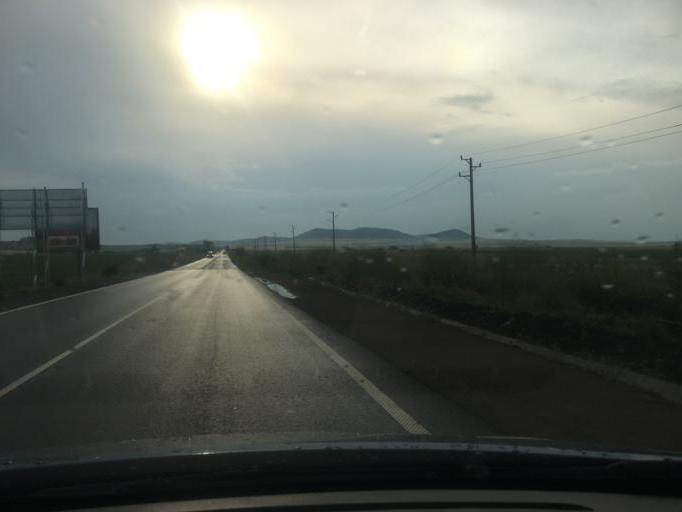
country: BG
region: Burgas
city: Aheloy
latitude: 42.6459
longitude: 27.6355
